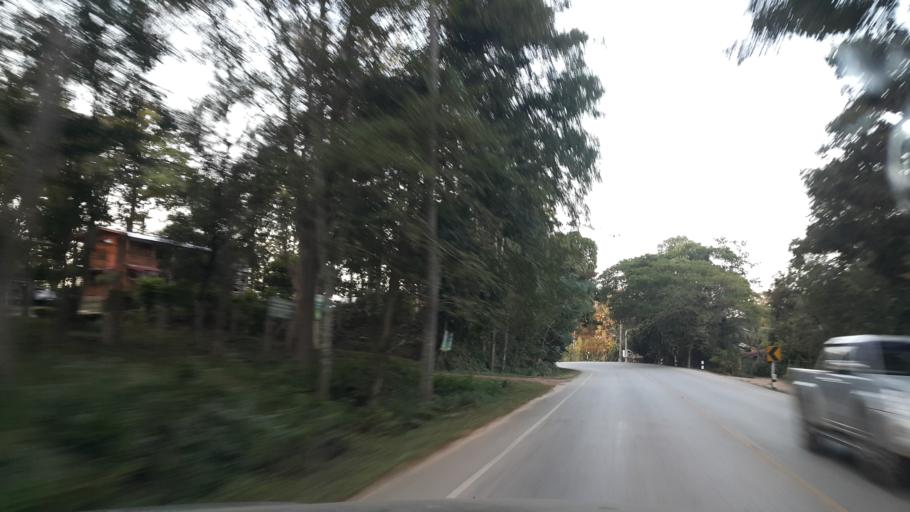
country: TH
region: Phrae
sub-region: Amphoe Wang Chin
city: Wang Chin
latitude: 17.8664
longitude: 99.6222
